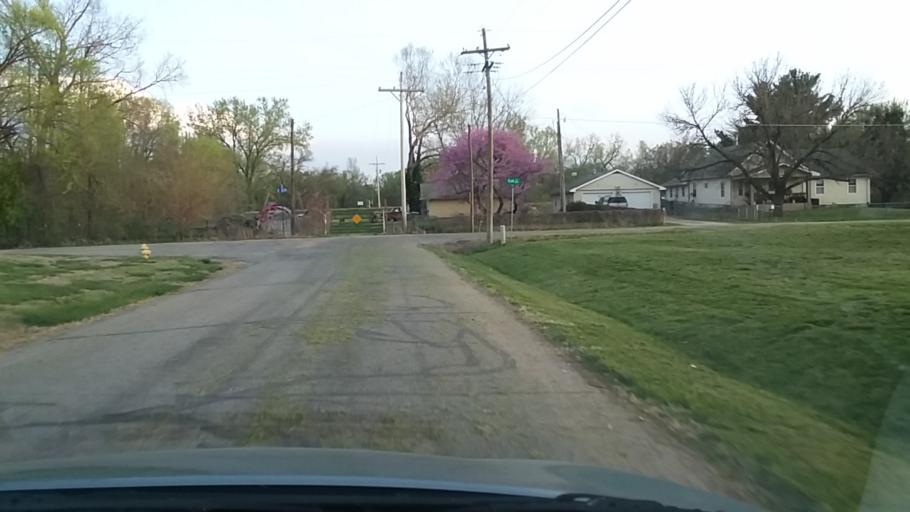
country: US
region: Kansas
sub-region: Douglas County
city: Lawrence
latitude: 38.9737
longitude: -95.2144
